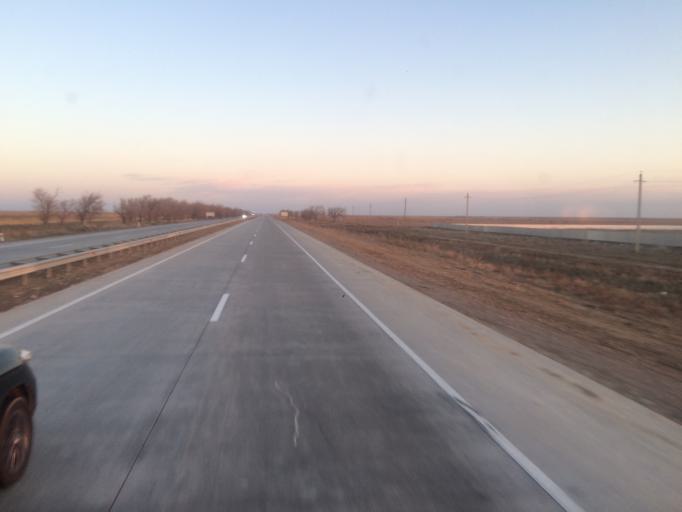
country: KZ
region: Ongtustik Qazaqstan
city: Bayaldyr
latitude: 43.0589
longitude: 68.6863
